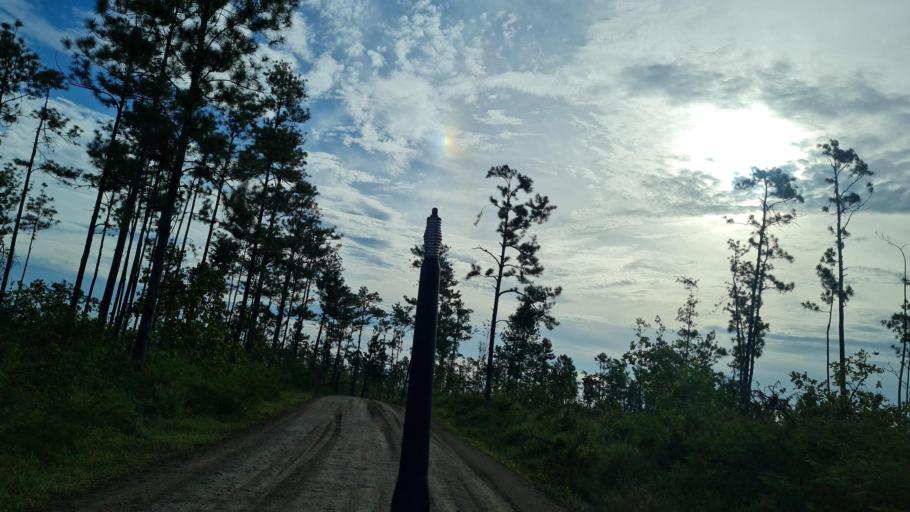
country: NI
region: Atlantico Sur
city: La Cruz de Rio Grande
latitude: 13.5624
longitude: -84.3053
